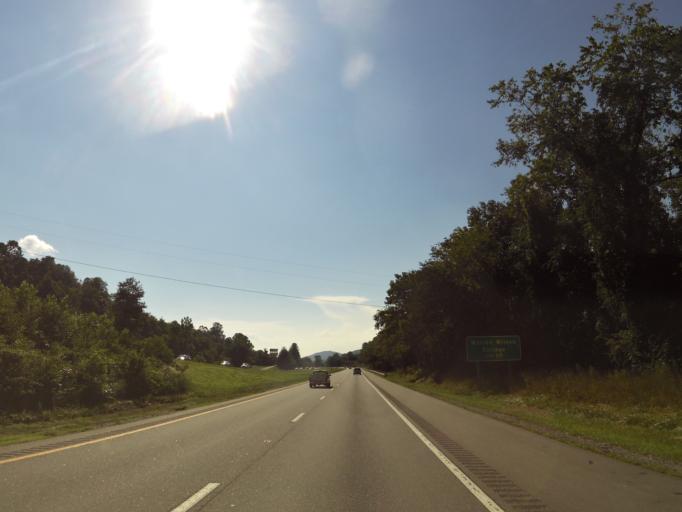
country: US
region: North Carolina
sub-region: Buncombe County
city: Swannanoa
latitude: 35.5987
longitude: -82.3825
